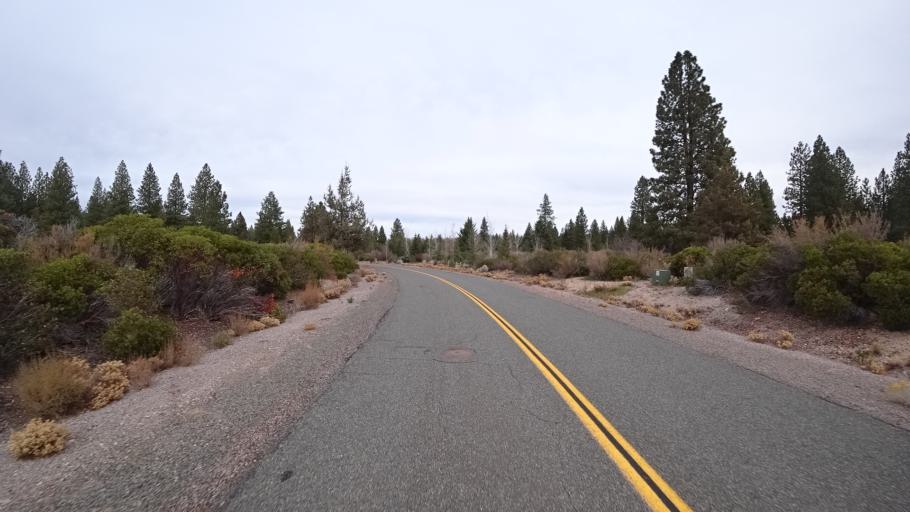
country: US
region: California
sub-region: Siskiyou County
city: Weed
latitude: 41.4116
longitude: -122.3647
